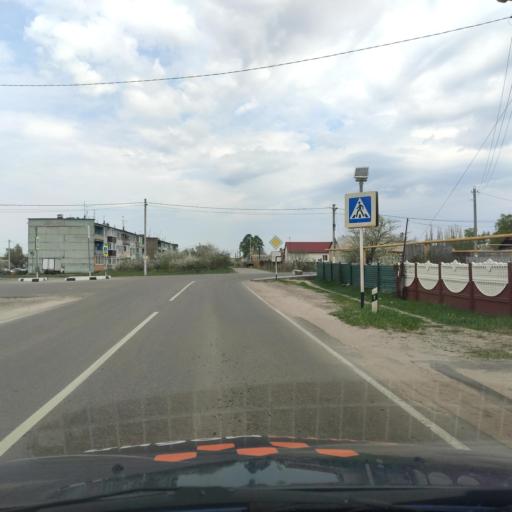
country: RU
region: Voronezj
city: Podgornoye
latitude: 51.8876
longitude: 39.1731
